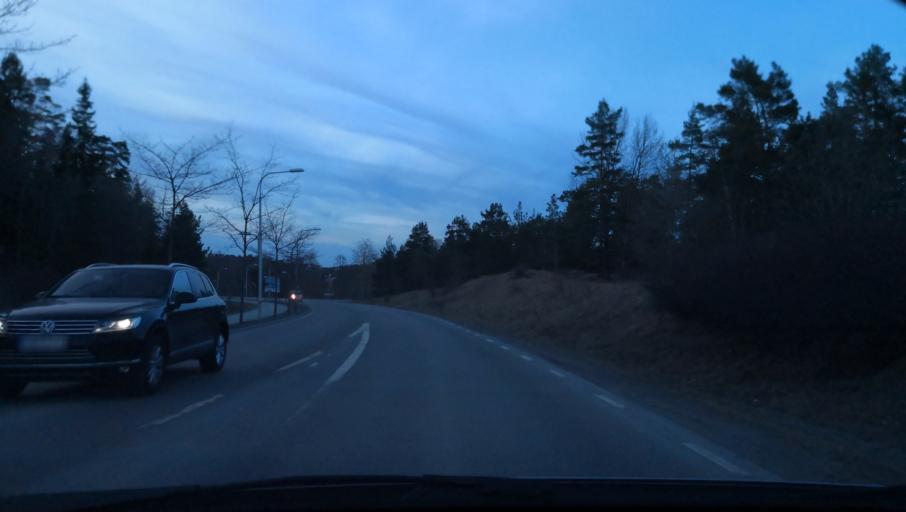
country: SE
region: Stockholm
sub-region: Varmdo Kommun
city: Gustavsberg
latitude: 59.3148
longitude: 18.3914
